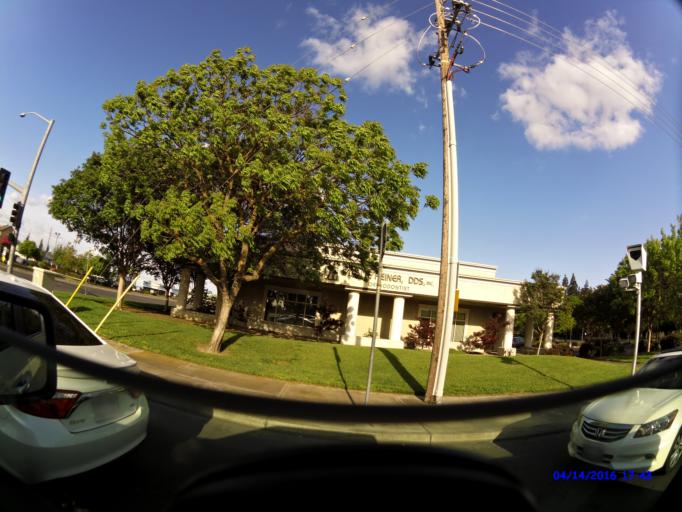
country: US
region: California
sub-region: Stanislaus County
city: Modesto
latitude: 37.6668
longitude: -120.9575
